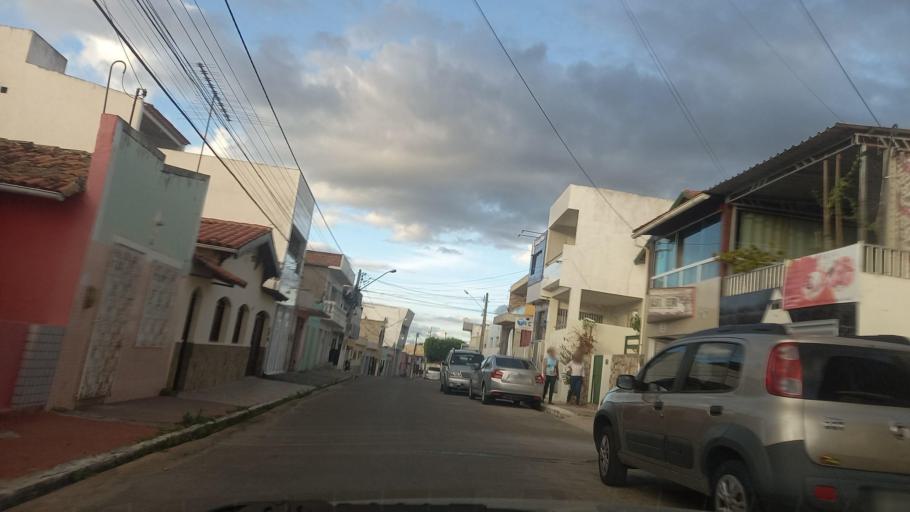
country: BR
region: Pernambuco
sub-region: Bezerros
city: Bezerros
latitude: -8.2361
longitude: -35.7540
